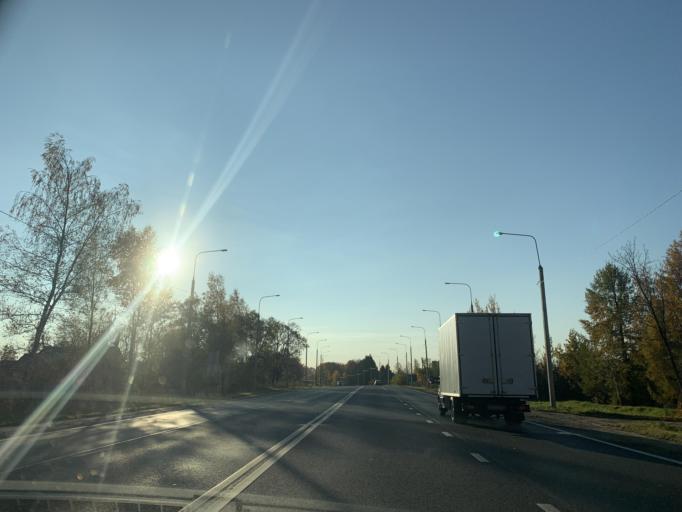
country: RU
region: Jaroslavl
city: Konstantinovskiy
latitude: 57.7701
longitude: 39.6708
